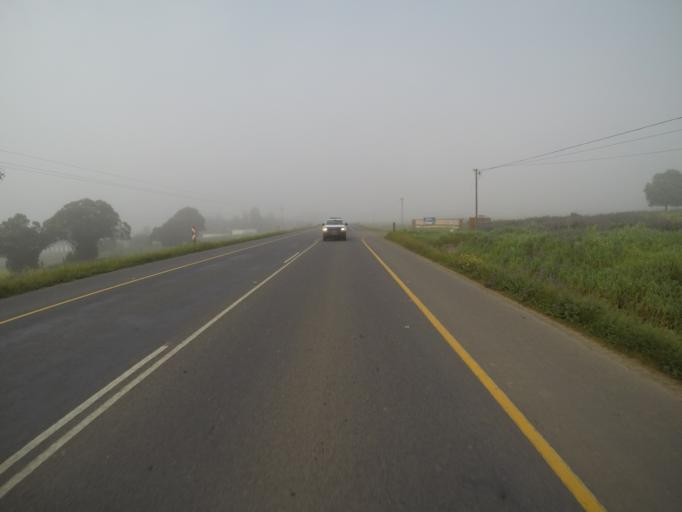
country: ZA
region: Western Cape
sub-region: City of Cape Town
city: Kraaifontein
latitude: -33.7706
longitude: 18.7112
